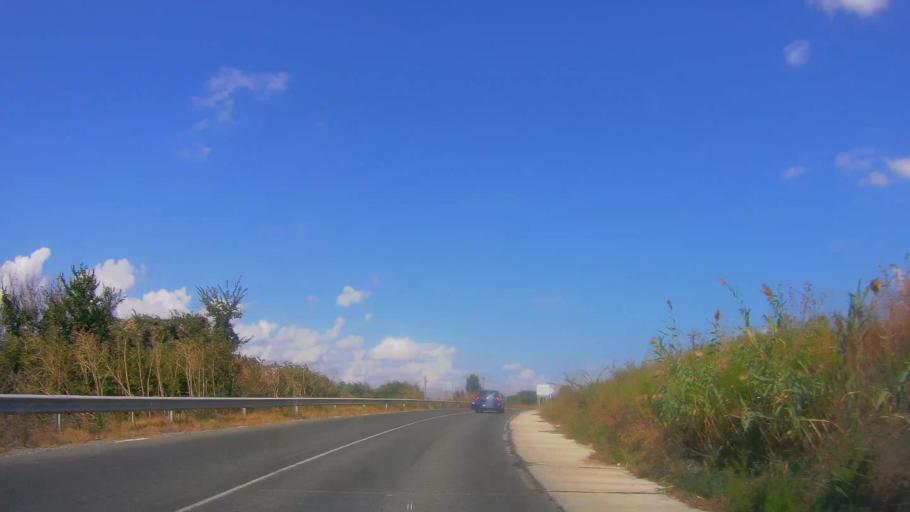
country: BG
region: Burgas
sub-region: Obshtina Burgas
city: Burgas
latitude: 42.4800
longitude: 27.3731
